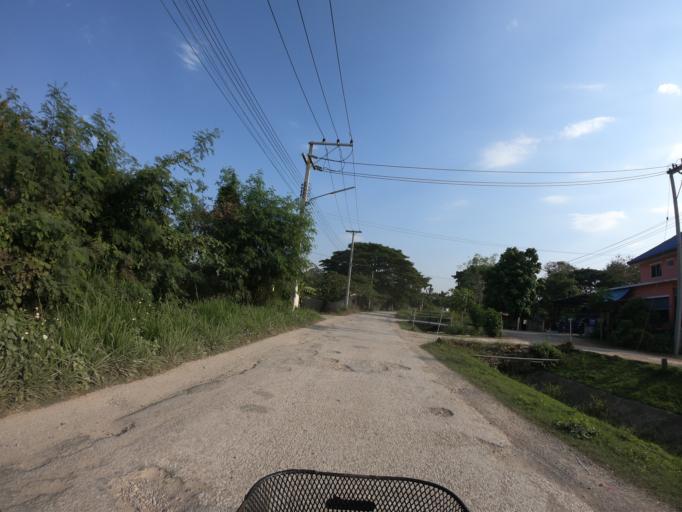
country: TH
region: Chiang Mai
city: Chiang Mai
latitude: 18.8278
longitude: 98.9925
